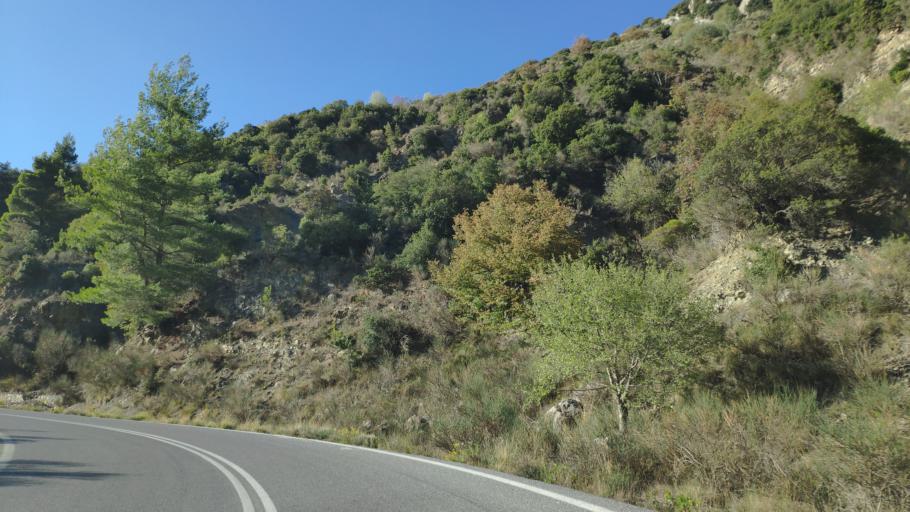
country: GR
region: Peloponnese
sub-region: Nomos Arkadias
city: Dimitsana
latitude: 37.5809
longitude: 22.0631
